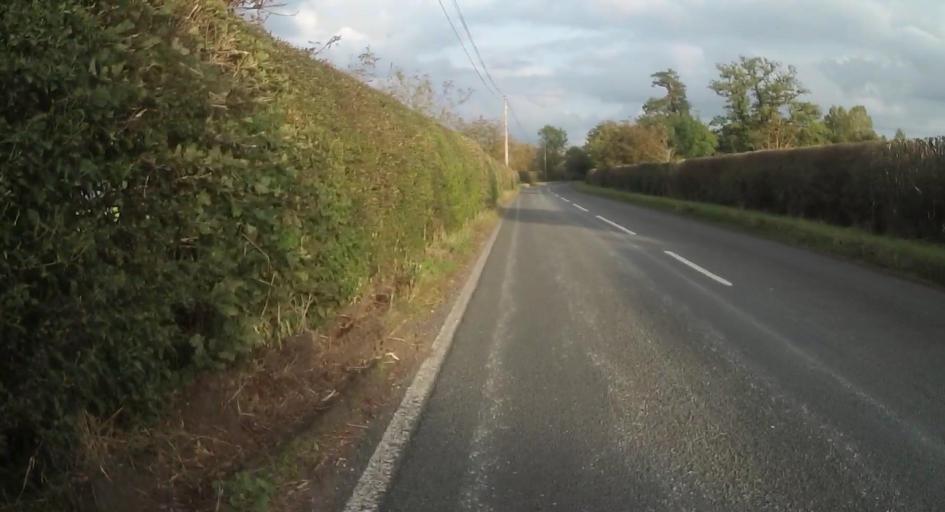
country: GB
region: England
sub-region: Hampshire
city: Tadley
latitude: 51.3808
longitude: -1.1753
